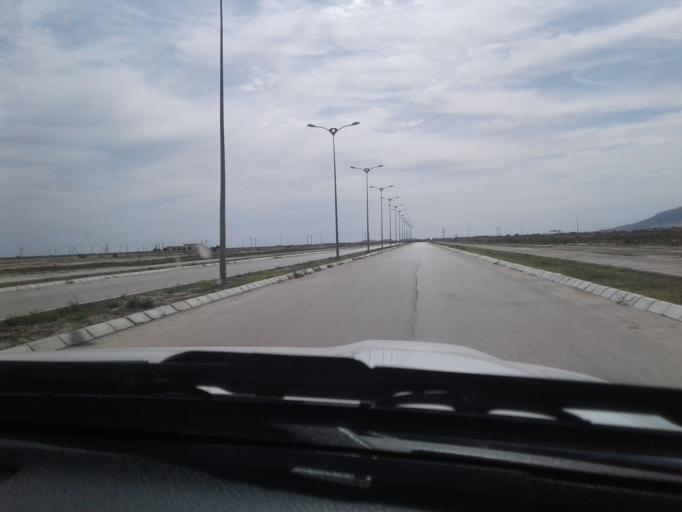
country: TM
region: Balkan
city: Gazanjyk
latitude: 39.2663
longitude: 55.4939
